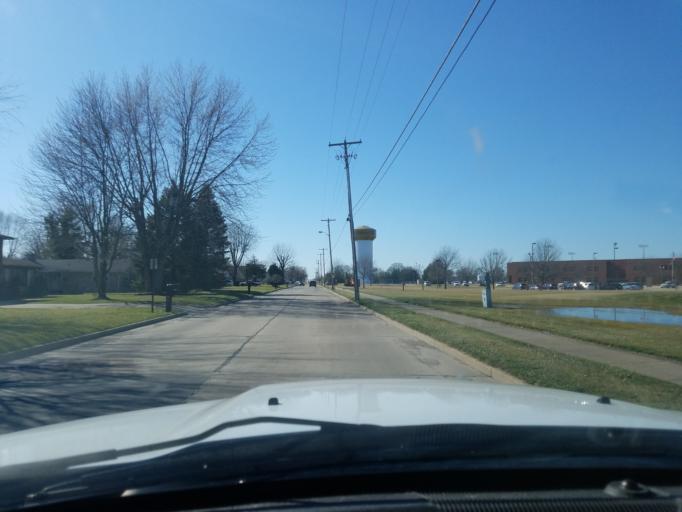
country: US
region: Indiana
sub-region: Shelby County
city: Shelbyville
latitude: 39.5047
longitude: -85.7914
